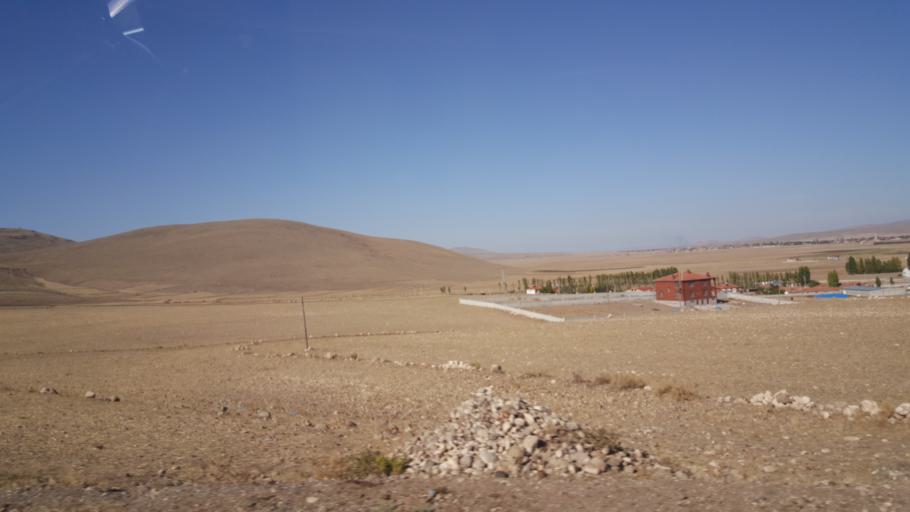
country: TR
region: Ankara
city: Altpinar
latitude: 39.1704
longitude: 32.7242
